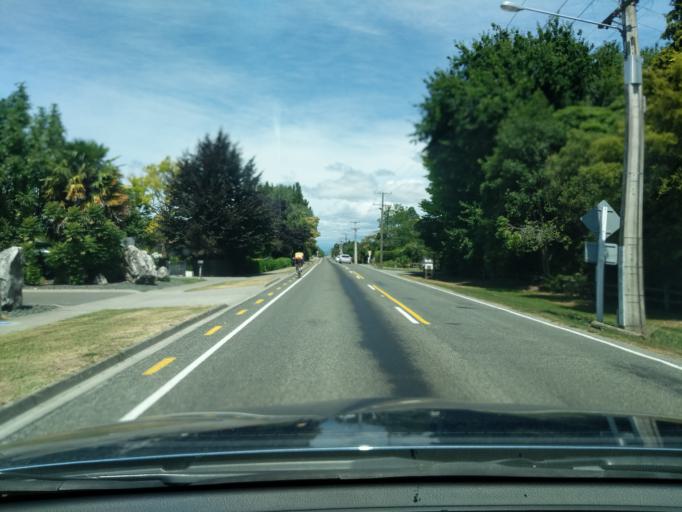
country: NZ
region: Tasman
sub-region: Tasman District
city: Motueka
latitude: -41.0777
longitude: 172.9974
